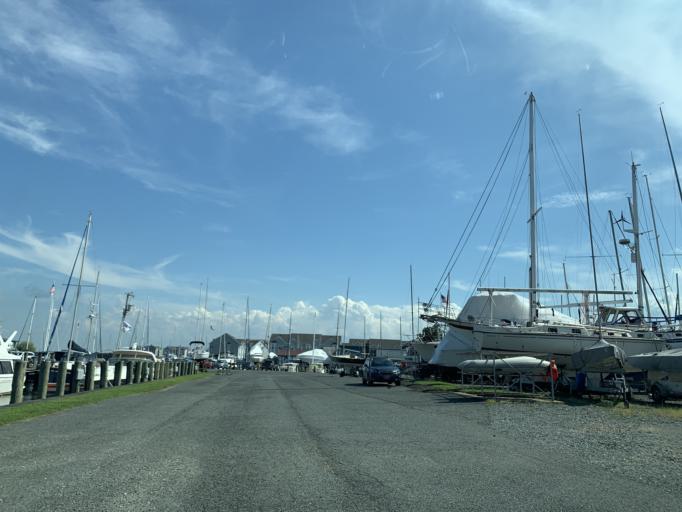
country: US
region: Maryland
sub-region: Harford County
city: Havre de Grace
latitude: 39.5474
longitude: -76.0861
